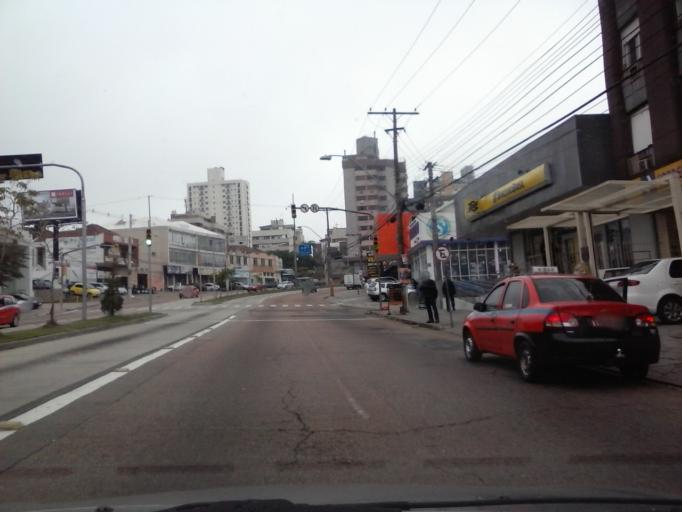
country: BR
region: Rio Grande do Sul
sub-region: Porto Alegre
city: Porto Alegre
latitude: -30.0409
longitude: -51.1687
